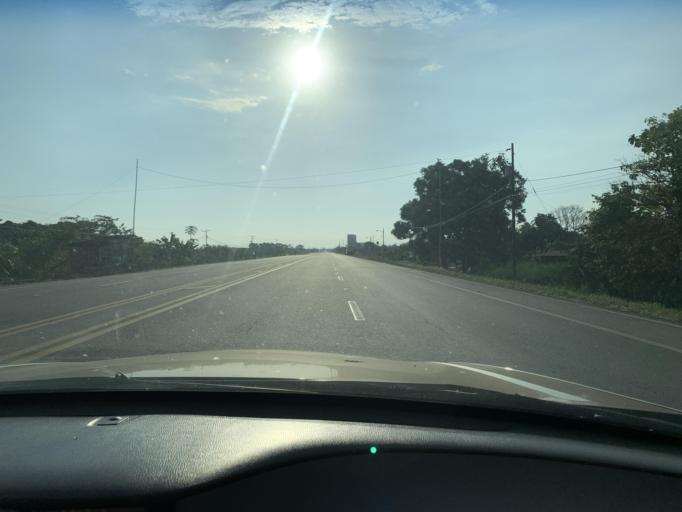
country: EC
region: Guayas
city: Naranjito
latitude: -2.2555
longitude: -79.6053
